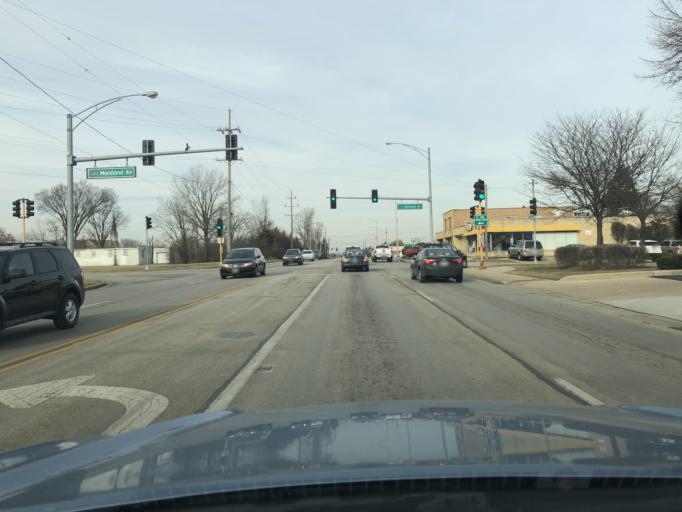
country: US
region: Illinois
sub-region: DuPage County
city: Addison
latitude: 41.9287
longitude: -87.9887
